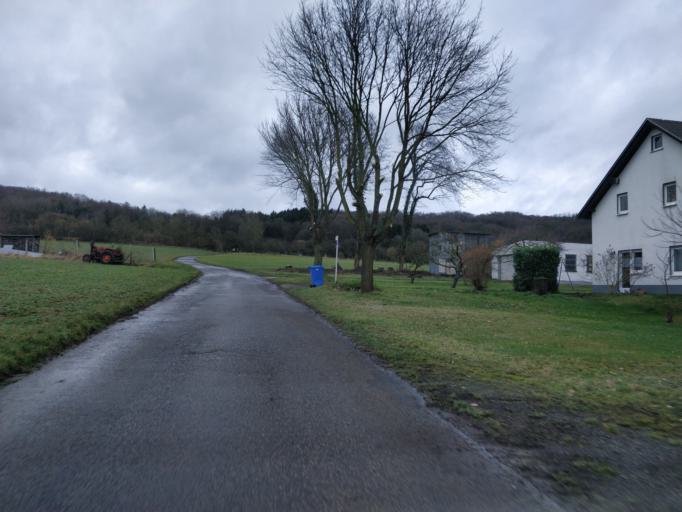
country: DE
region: Rheinland-Pfalz
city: Leutesdorf
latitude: 50.4581
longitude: 7.4057
